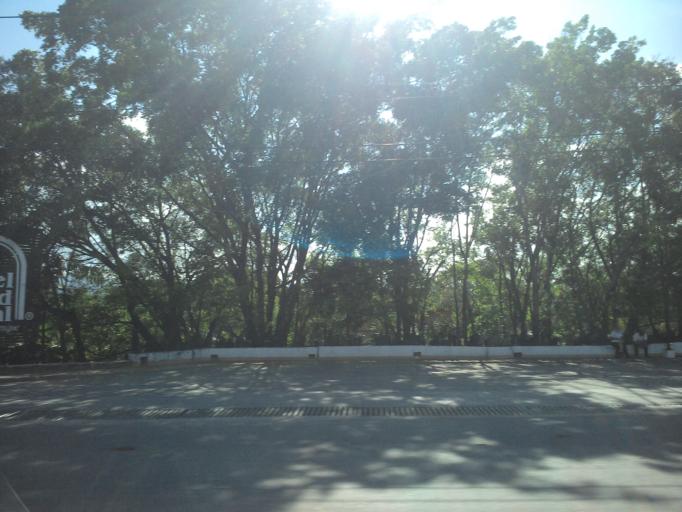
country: MX
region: Chiapas
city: Palenque
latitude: 17.5160
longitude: -91.9934
